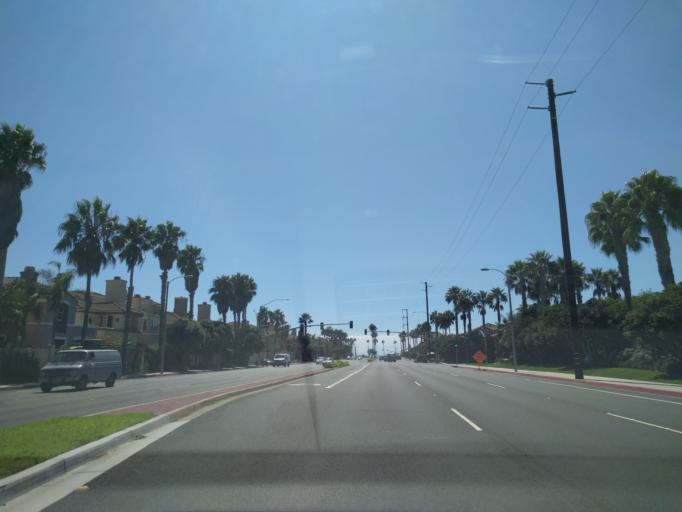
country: US
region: California
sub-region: Orange County
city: Huntington Beach
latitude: 33.6716
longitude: -118.0140
